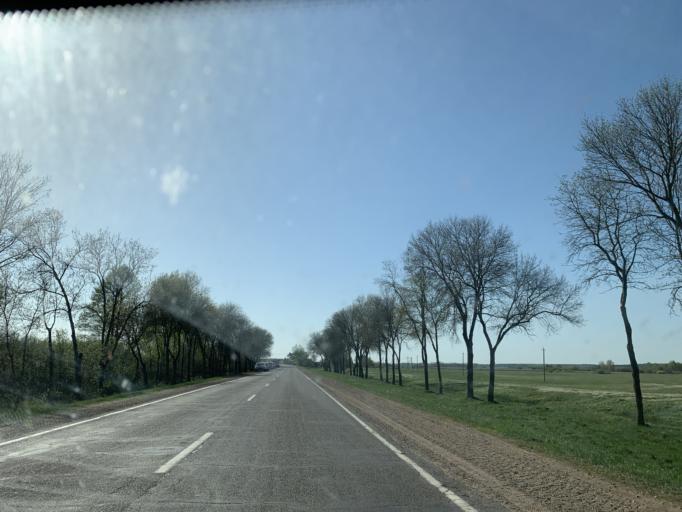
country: BY
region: Minsk
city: Nyasvizh
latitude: 53.2292
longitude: 26.7391
